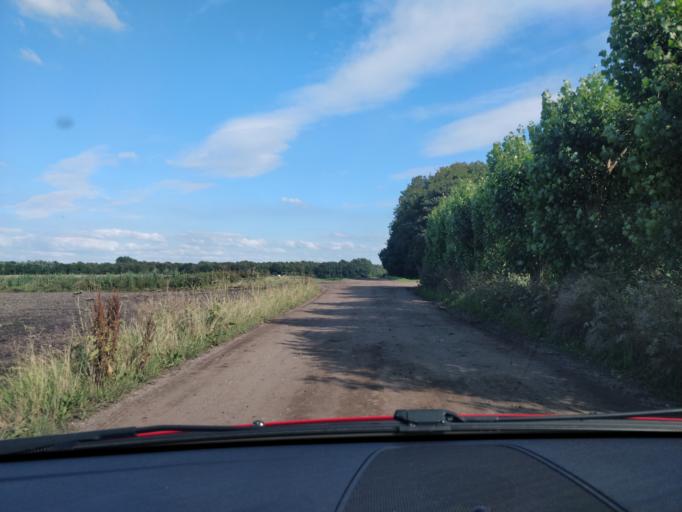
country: GB
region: England
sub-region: Lancashire
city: Banks
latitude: 53.6568
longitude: -2.9066
